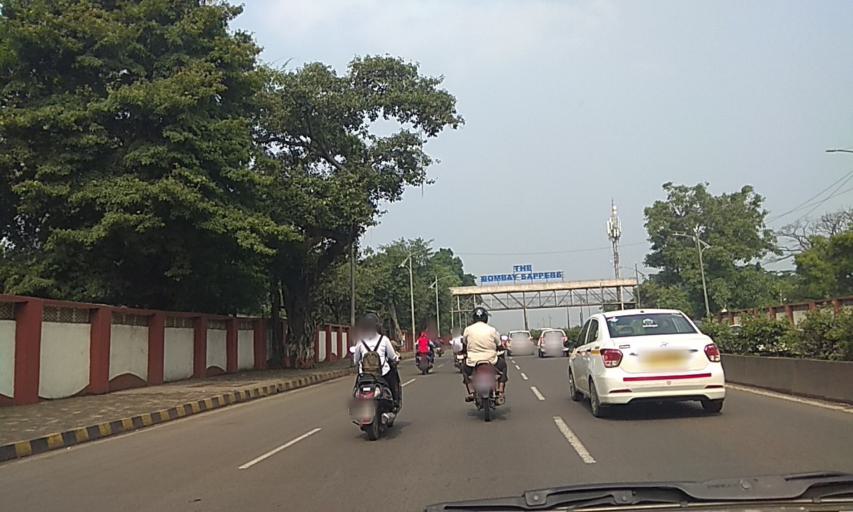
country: IN
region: Maharashtra
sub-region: Pune Division
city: Khadki
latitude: 18.5499
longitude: 73.8692
